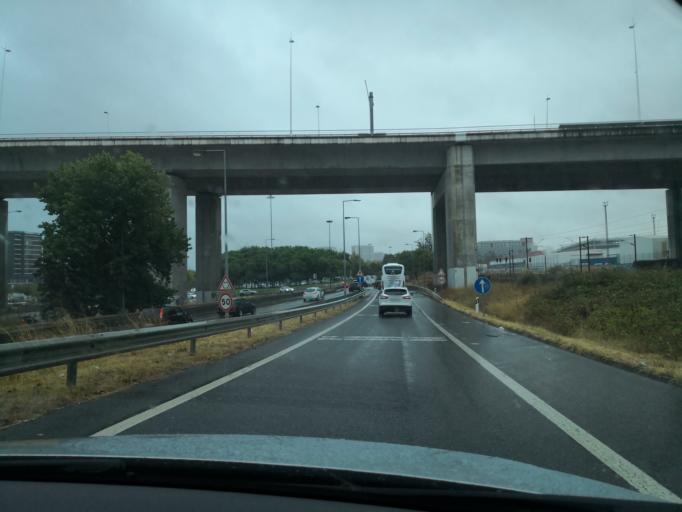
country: PT
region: Lisbon
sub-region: Loures
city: Moscavide
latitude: 38.7873
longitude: -9.1005
